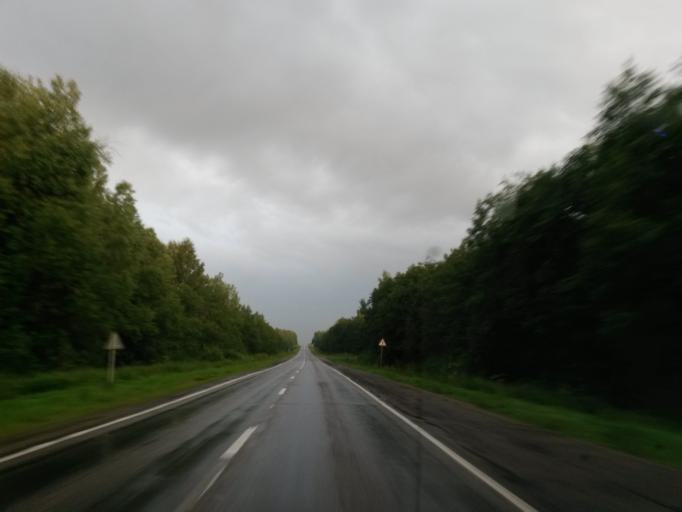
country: RU
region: Jaroslavl
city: Yaroslavl
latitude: 57.4893
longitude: 39.9017
